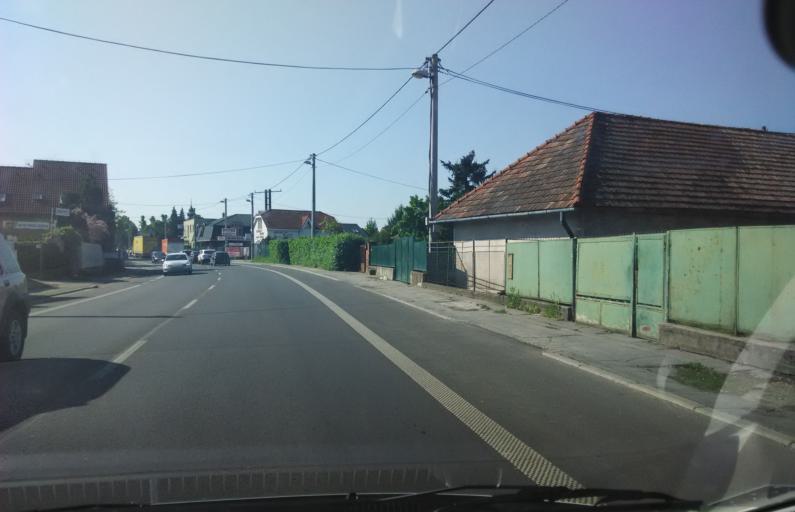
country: SK
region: Nitriansky
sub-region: Okres Nitra
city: Nitra
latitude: 48.2752
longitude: 18.0978
